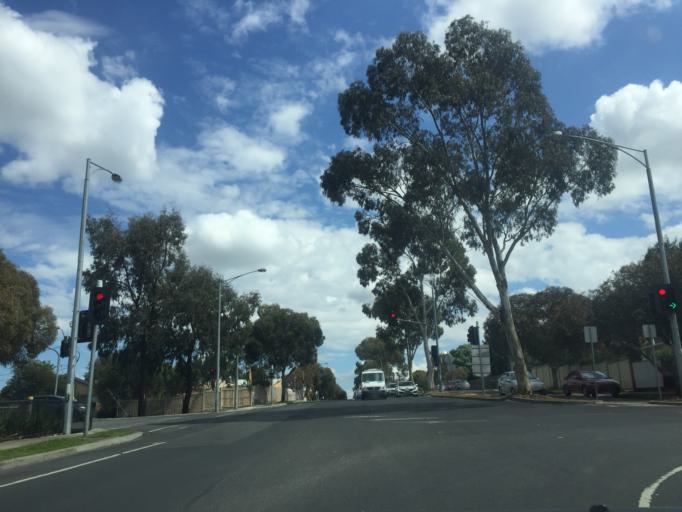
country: AU
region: Victoria
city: Heidelberg West
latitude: -37.7361
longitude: 145.0288
